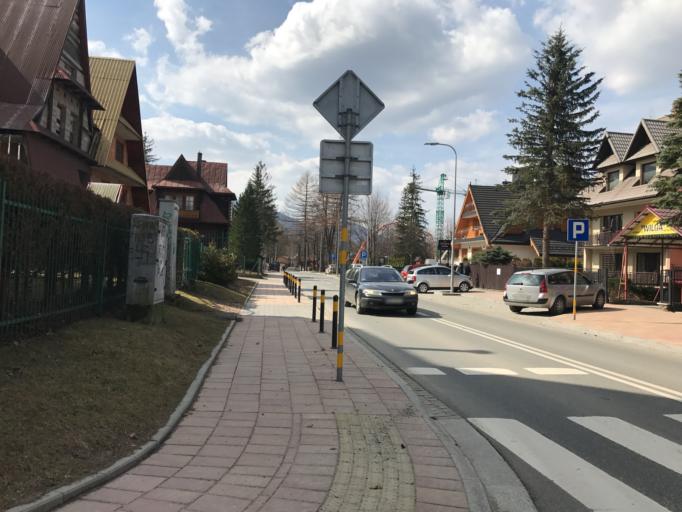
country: PL
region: Lesser Poland Voivodeship
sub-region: Powiat tatrzanski
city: Zakopane
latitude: 49.2874
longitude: 19.9656
